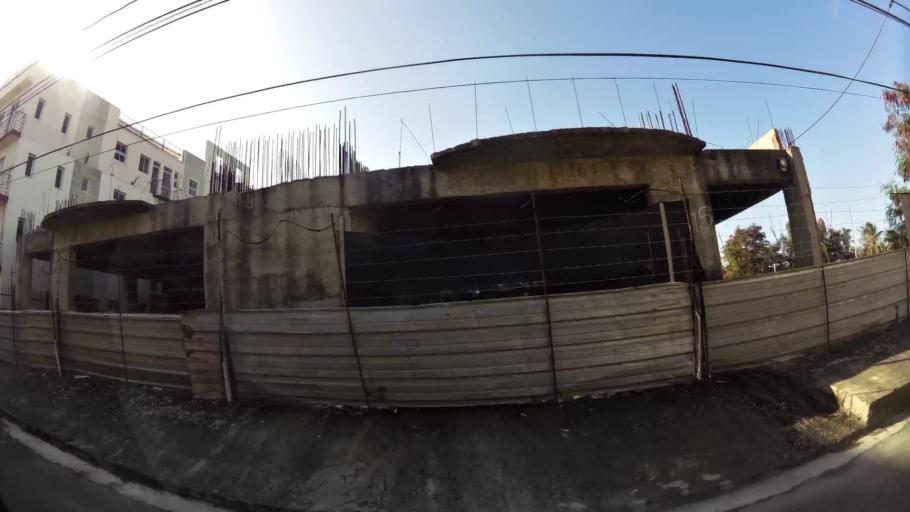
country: DO
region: Santo Domingo
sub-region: Santo Domingo
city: Santo Domingo Este
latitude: 18.4698
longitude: -69.8604
